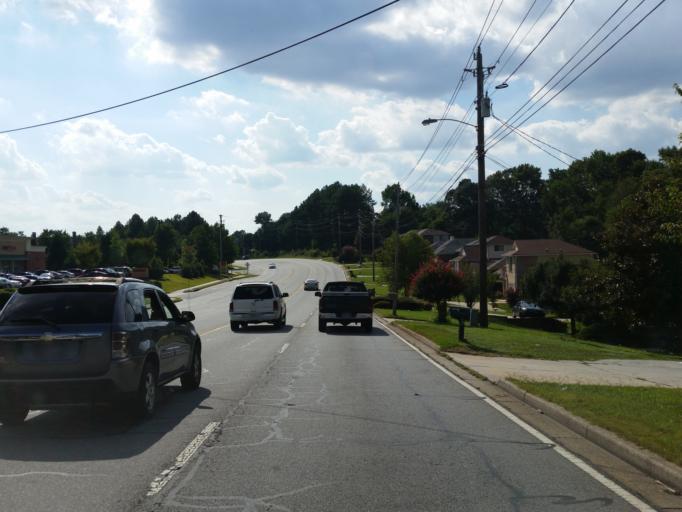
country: US
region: Georgia
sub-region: Gwinnett County
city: Duluth
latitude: 33.9497
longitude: -84.0834
